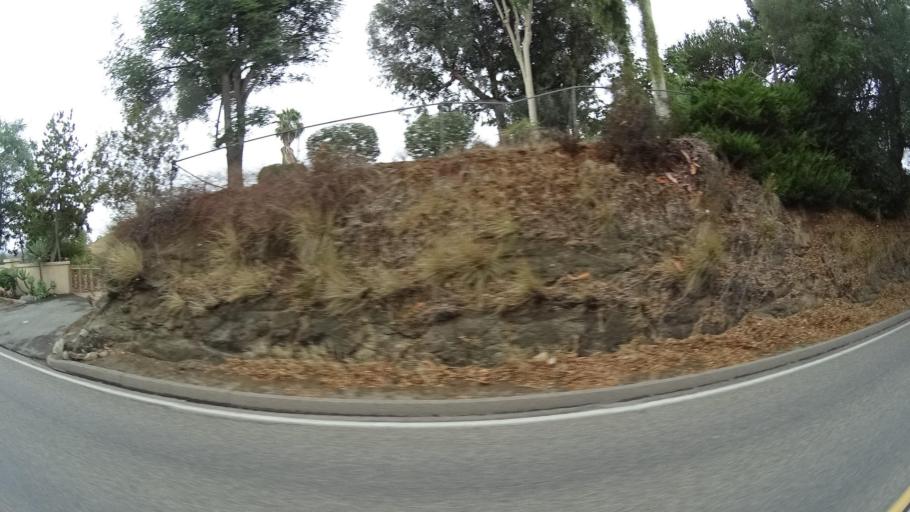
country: US
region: California
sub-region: San Diego County
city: Escondido
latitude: 33.0859
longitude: -117.1081
